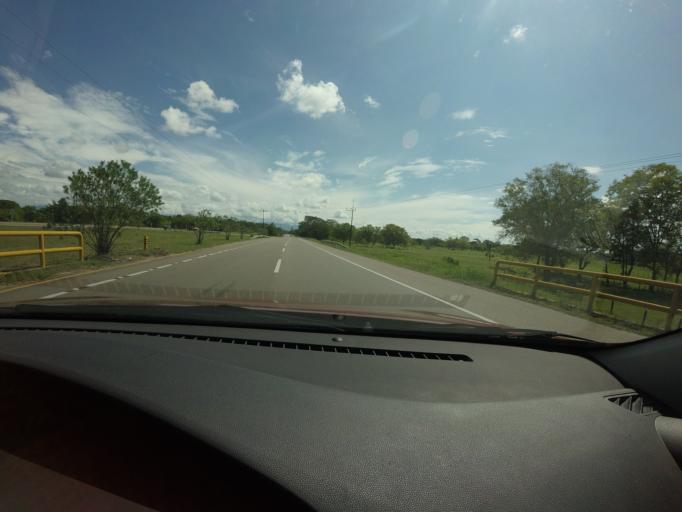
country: CO
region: Antioquia
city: Puerto Triunfo
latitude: 5.7476
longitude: -74.6270
